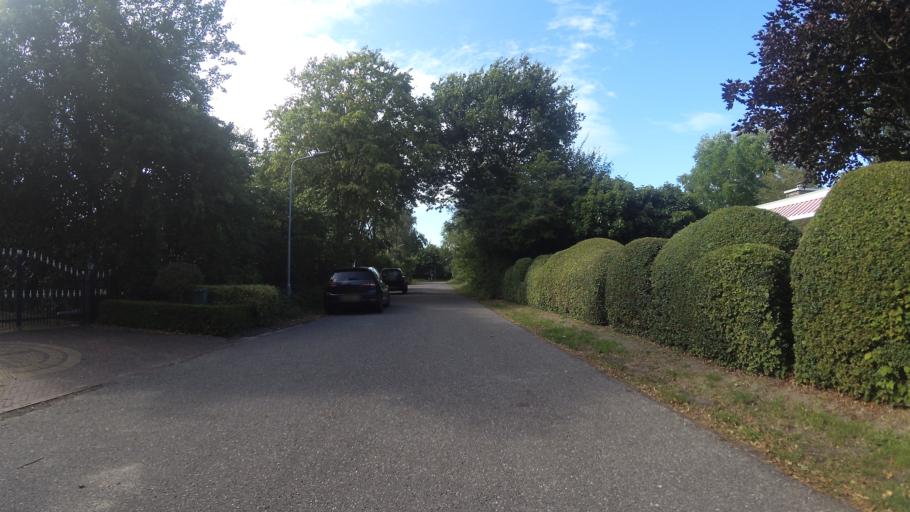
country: NL
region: Zeeland
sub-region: Gemeente Middelburg
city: Middelburg
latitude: 51.5749
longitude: 3.5430
